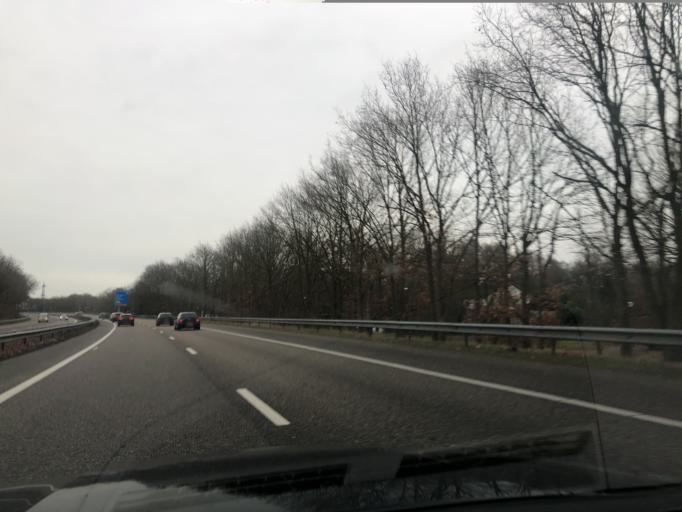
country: NL
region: North Brabant
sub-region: Gemeente Bernheze
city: Heesch
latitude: 51.7329
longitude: 5.5587
